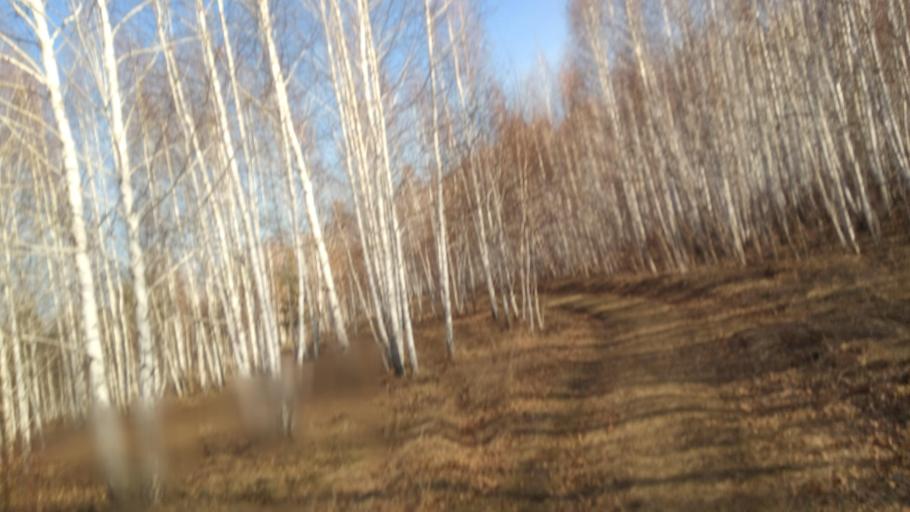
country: RU
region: Chelyabinsk
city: Sargazy
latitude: 55.1153
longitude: 61.2408
